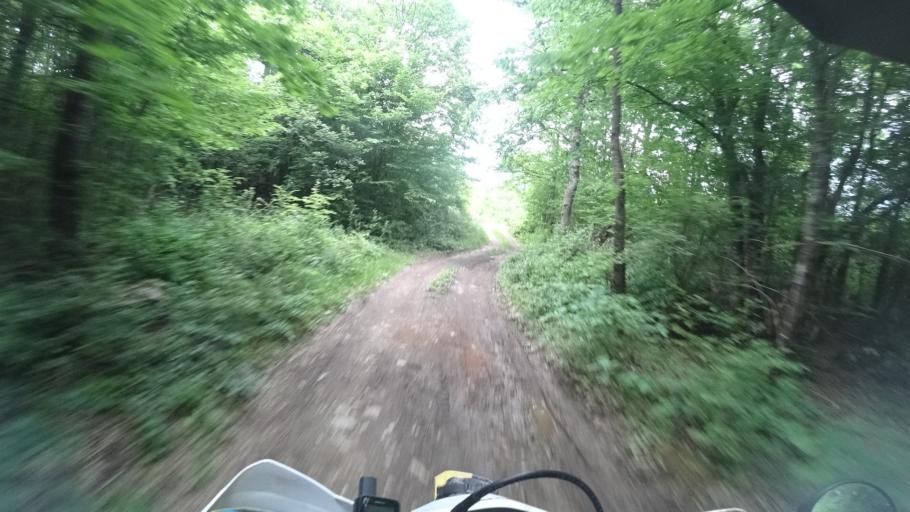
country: HR
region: Zadarska
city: Obrovac
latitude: 44.3439
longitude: 15.6518
